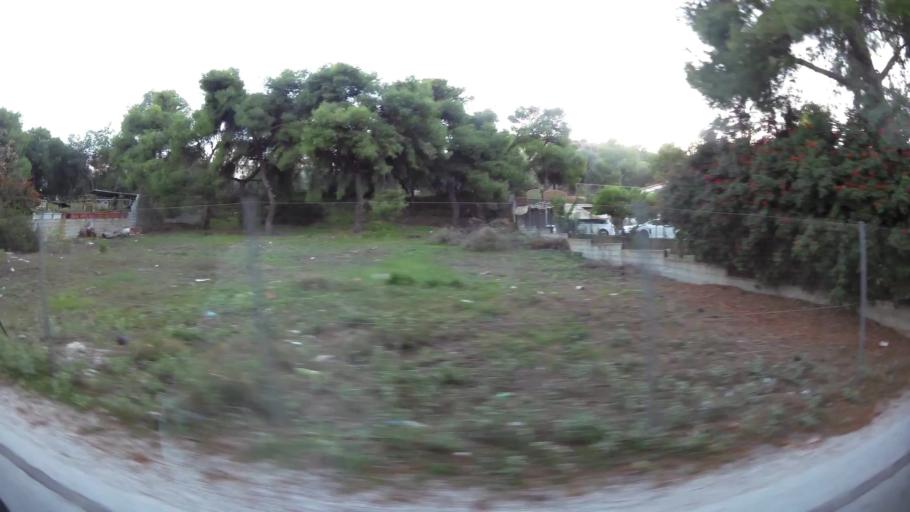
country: GR
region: Attica
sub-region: Nomarchia Anatolikis Attikis
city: Vouliagmeni
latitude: 37.8212
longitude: 23.7931
